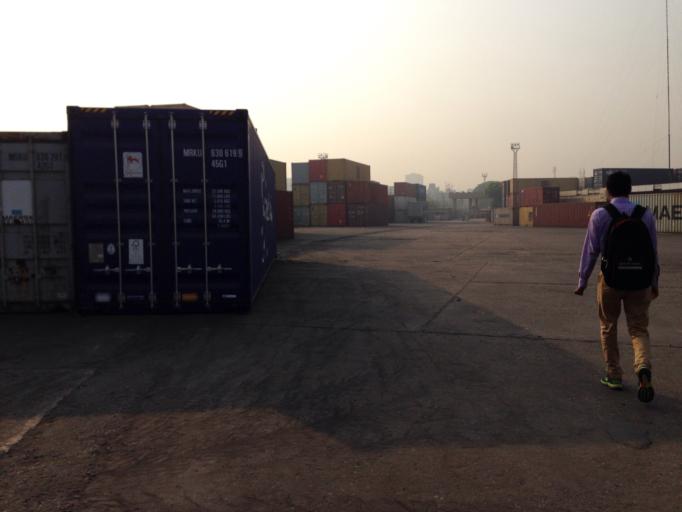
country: BD
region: Dhaka
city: Paltan
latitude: 23.7272
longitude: 90.4267
